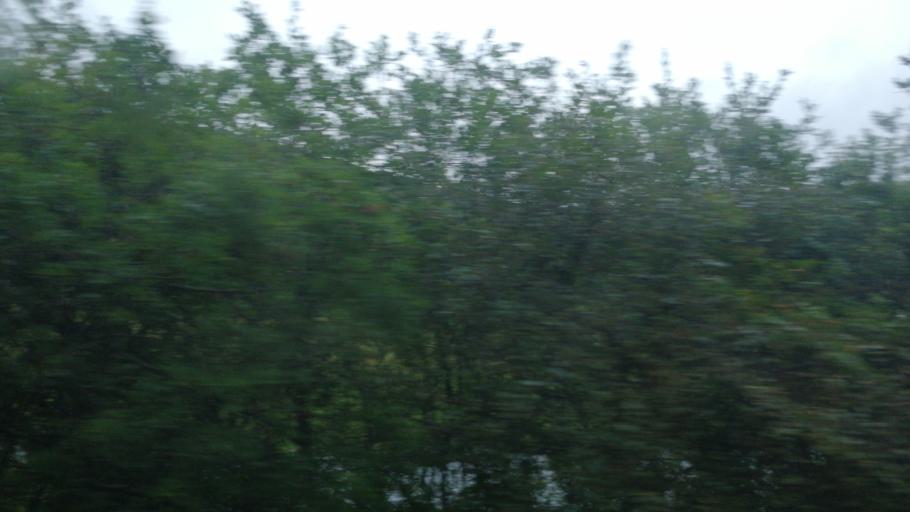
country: GB
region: Scotland
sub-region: Highland
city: Brora
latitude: 58.1348
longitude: -3.6838
